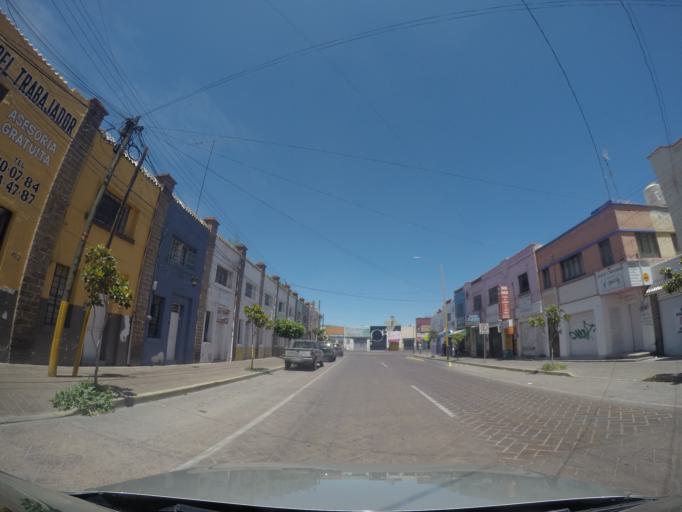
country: MX
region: San Luis Potosi
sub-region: San Luis Potosi
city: San Luis Potosi
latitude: 22.1545
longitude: -100.9822
